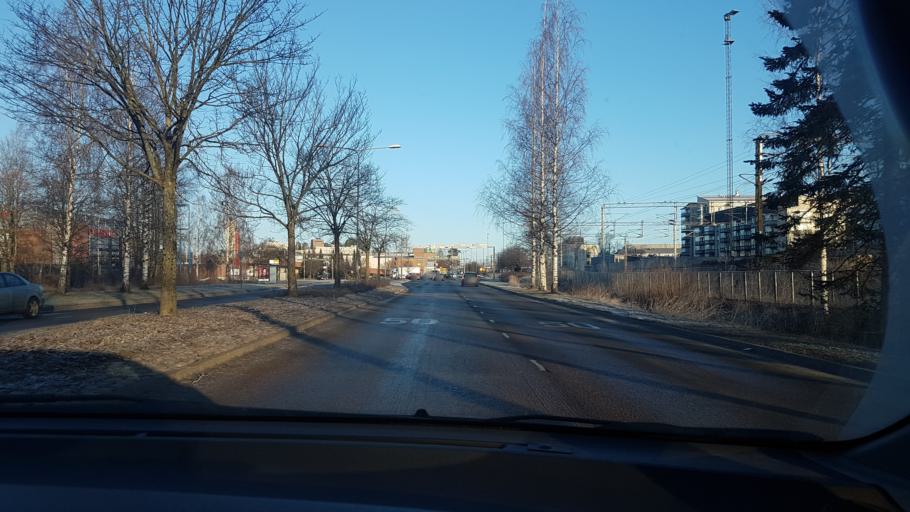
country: FI
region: Uusimaa
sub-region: Helsinki
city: Kerava
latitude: 60.3981
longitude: 25.1032
